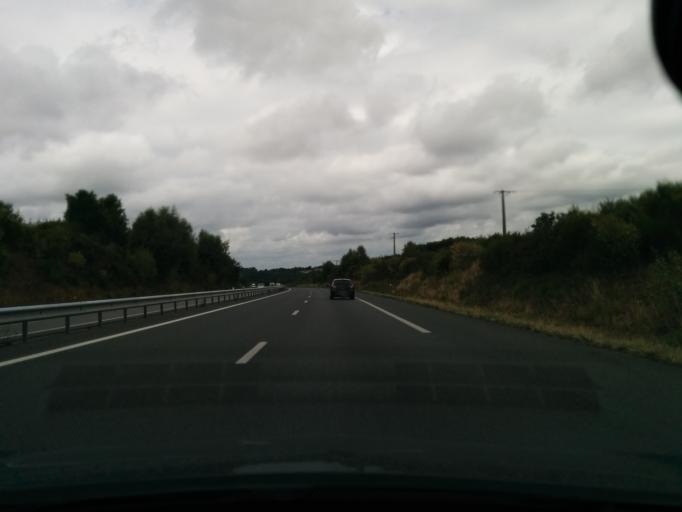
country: FR
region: Limousin
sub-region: Departement de la Haute-Vienne
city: Vicq-sur-Breuilh
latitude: 45.6554
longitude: 1.4022
